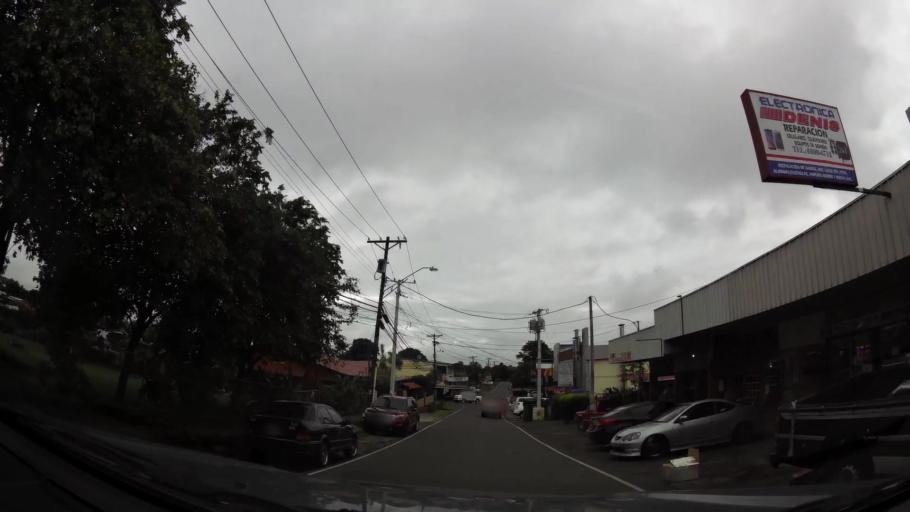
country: PA
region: Chiriqui
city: La Concepcion
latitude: 8.5161
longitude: -82.6197
